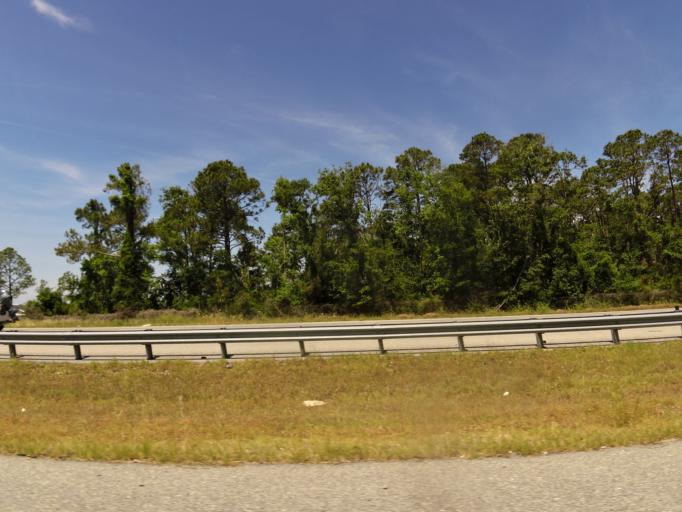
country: US
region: Georgia
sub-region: Glynn County
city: Dock Junction
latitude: 31.1741
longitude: -81.5490
